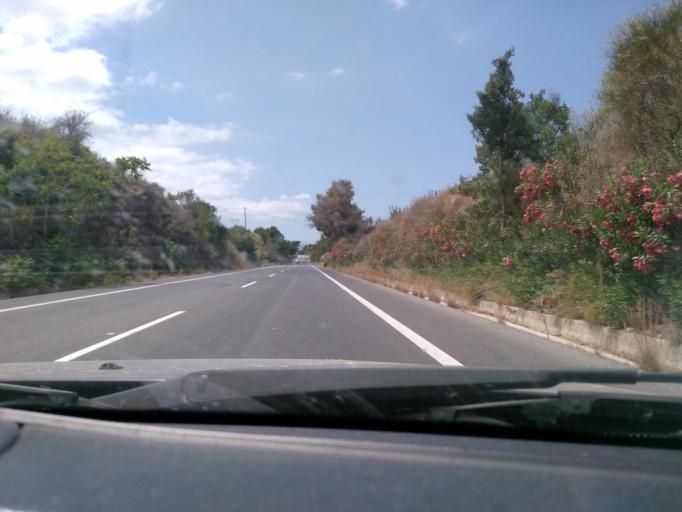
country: GR
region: Crete
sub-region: Nomos Chanias
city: Georgioupolis
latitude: 35.3639
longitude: 24.2387
